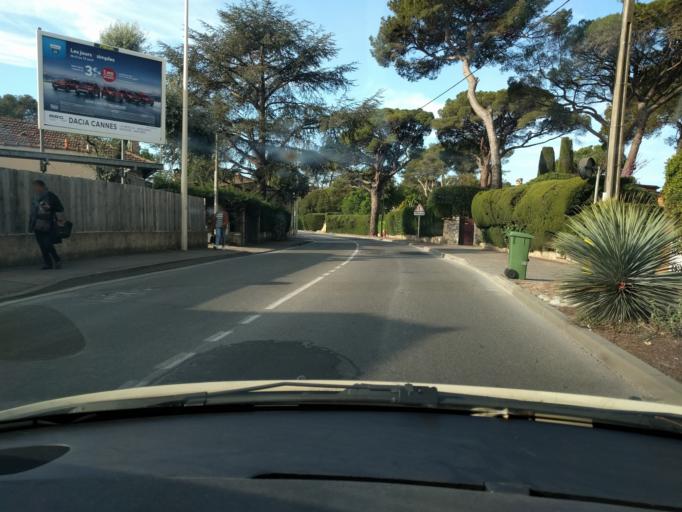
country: FR
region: Provence-Alpes-Cote d'Azur
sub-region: Departement des Alpes-Maritimes
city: Mougins
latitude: 43.5725
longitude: 6.9833
